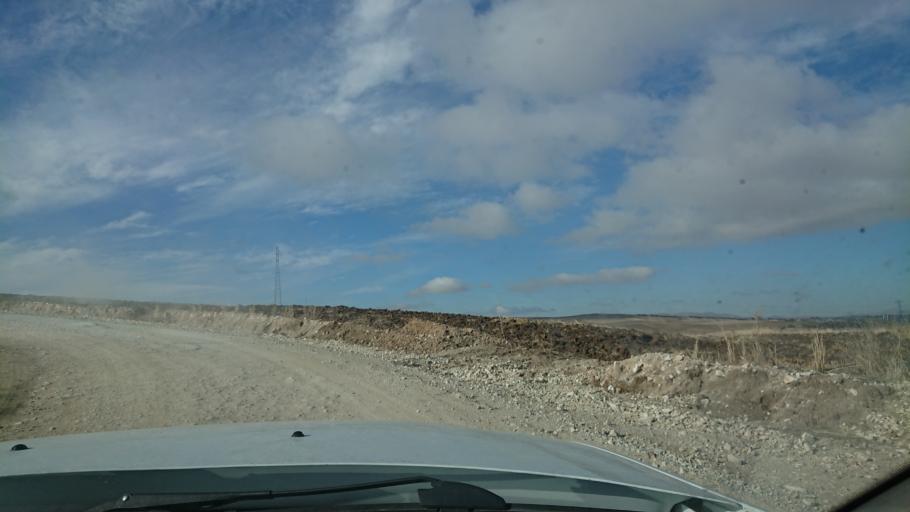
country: TR
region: Aksaray
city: Agacoren
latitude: 38.8494
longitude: 33.9468
